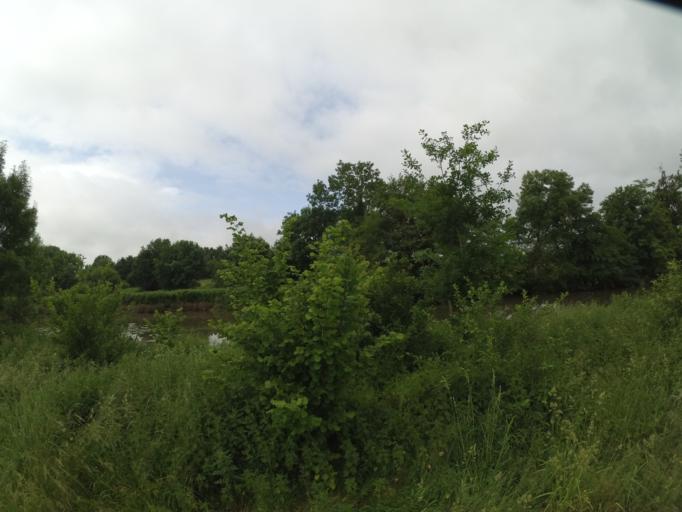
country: FR
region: Pays de la Loire
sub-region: Departement de la Vendee
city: Nesmy
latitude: 46.6247
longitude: -1.4183
